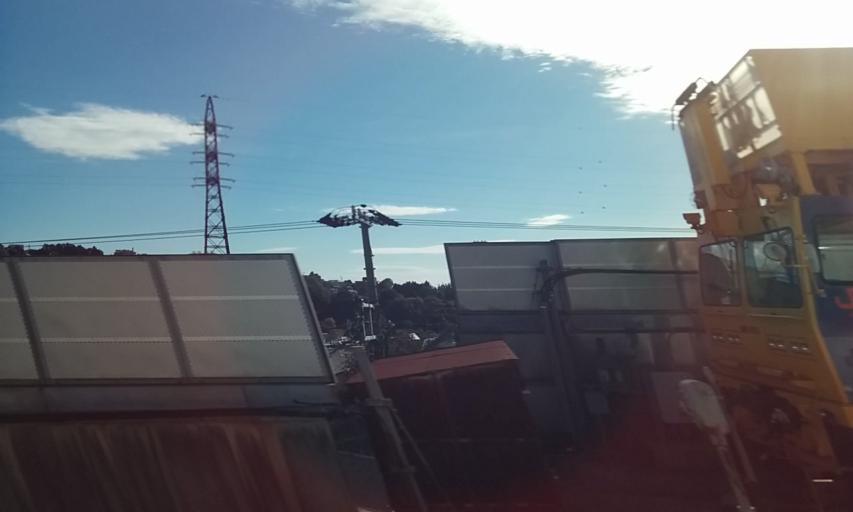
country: JP
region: Kanagawa
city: Yugawara
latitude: 35.1520
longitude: 139.1038
